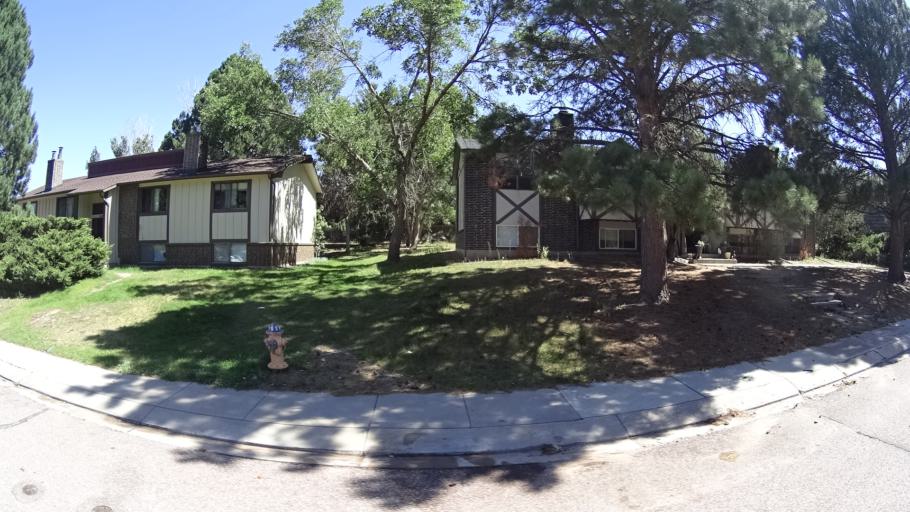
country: US
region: Colorado
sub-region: El Paso County
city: Air Force Academy
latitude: 38.9246
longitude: -104.8071
